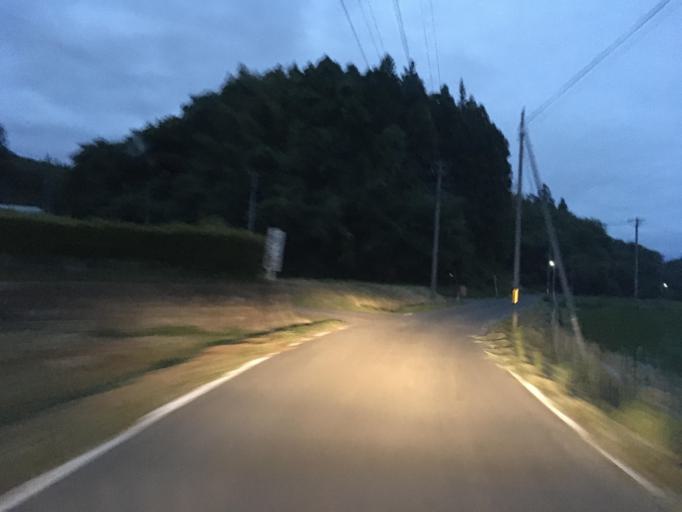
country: JP
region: Miyagi
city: Furukawa
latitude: 38.7861
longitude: 140.9279
